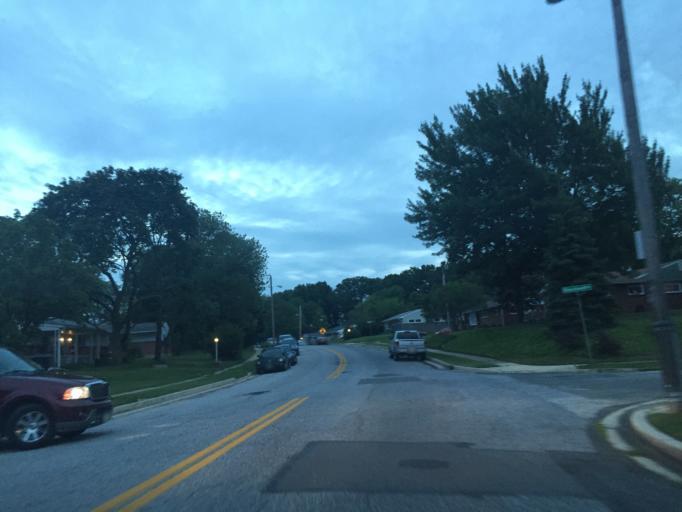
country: US
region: Maryland
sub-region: Baltimore County
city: Carney
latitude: 39.3937
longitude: -76.5349
